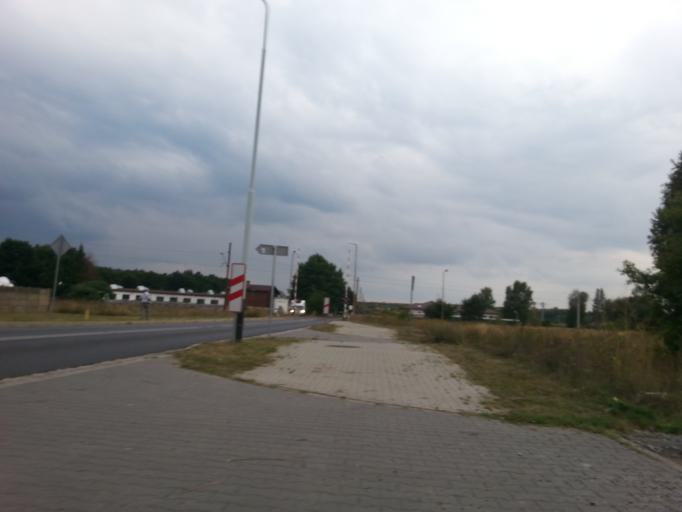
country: PL
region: Lower Silesian Voivodeship
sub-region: Powiat olesnicki
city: Twardogora
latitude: 51.3602
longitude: 17.4565
